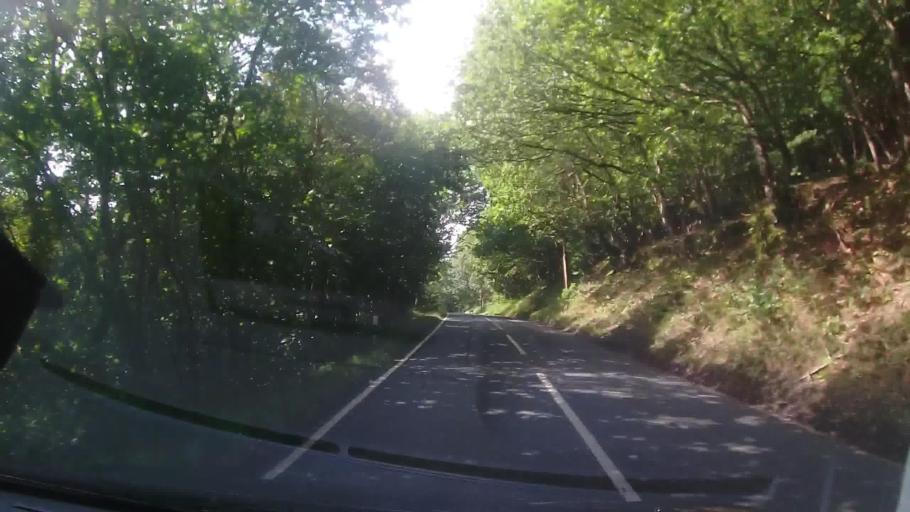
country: GB
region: Wales
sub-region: Sir Powys
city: Knighton
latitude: 52.3556
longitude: -3.0379
